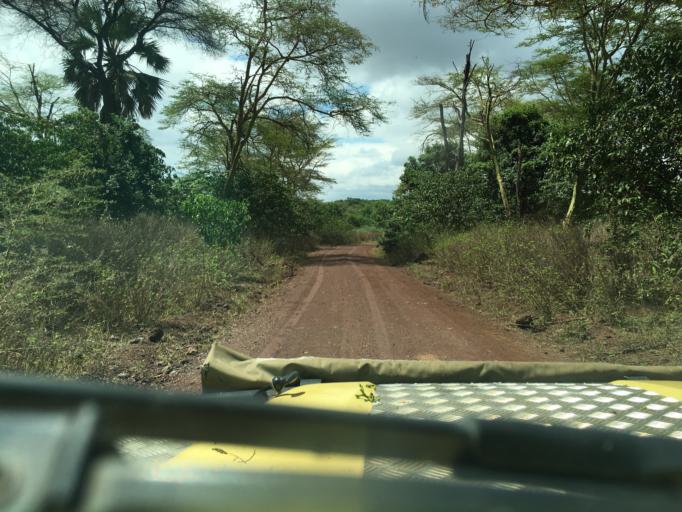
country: TZ
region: Arusha
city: Mto wa Mbu
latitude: -3.4190
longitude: 35.8190
